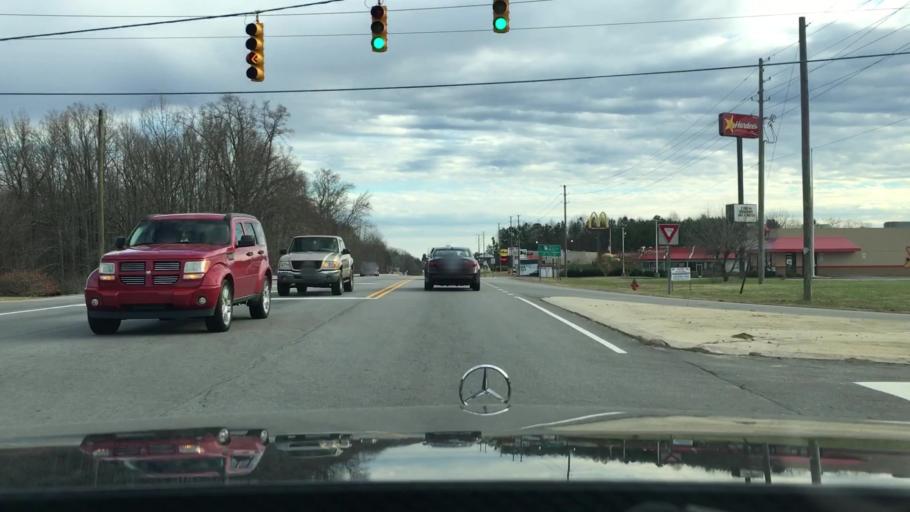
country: US
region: North Carolina
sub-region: Caswell County
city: Yanceyville
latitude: 36.4187
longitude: -79.3507
